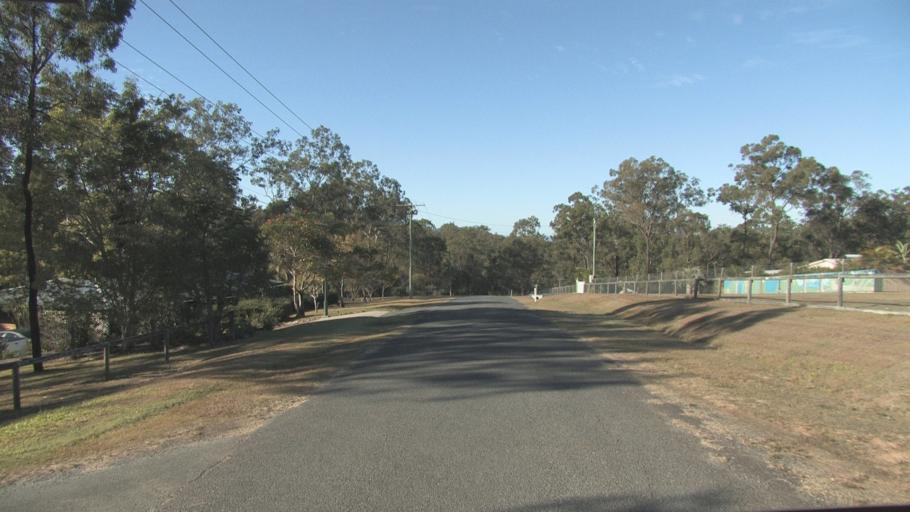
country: AU
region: Queensland
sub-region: Logan
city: Cedar Vale
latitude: -27.8353
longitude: 153.0881
